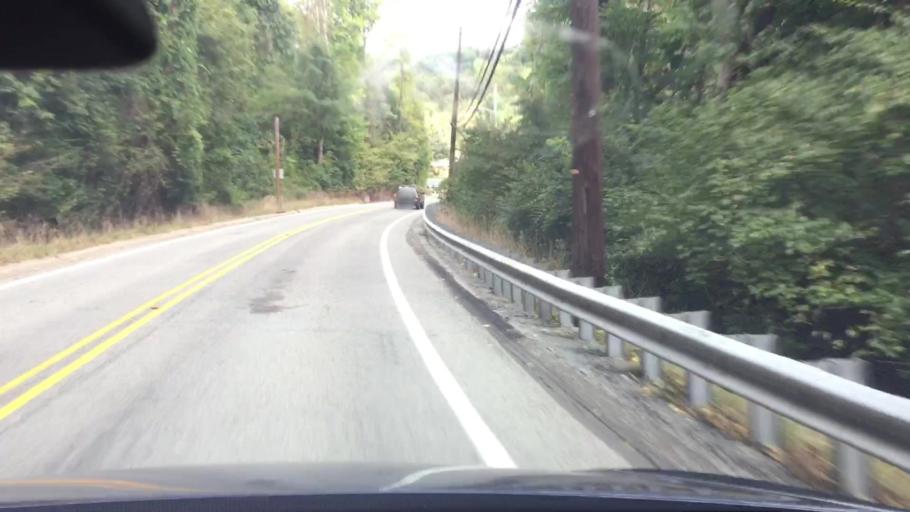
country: US
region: Pennsylvania
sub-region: Allegheny County
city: Cheswick
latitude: 40.5037
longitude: -79.7946
